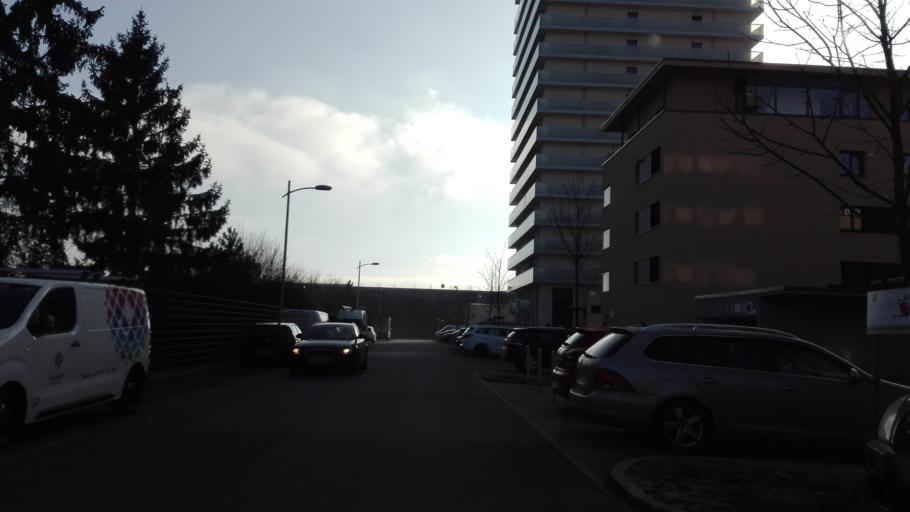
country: AT
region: Upper Austria
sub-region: Politischer Bezirk Linz-Land
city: Leonding
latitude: 48.2579
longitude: 14.2852
